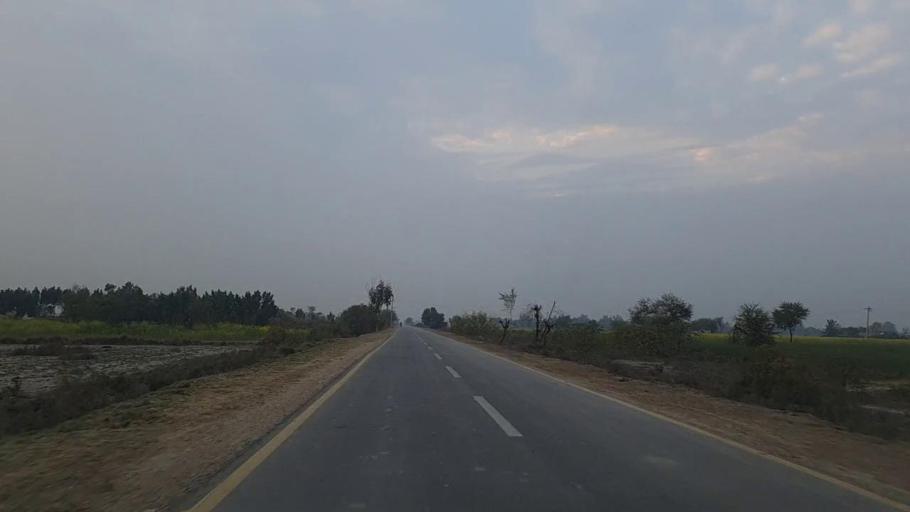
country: PK
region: Sindh
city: Jam Sahib
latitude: 26.3131
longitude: 68.5805
